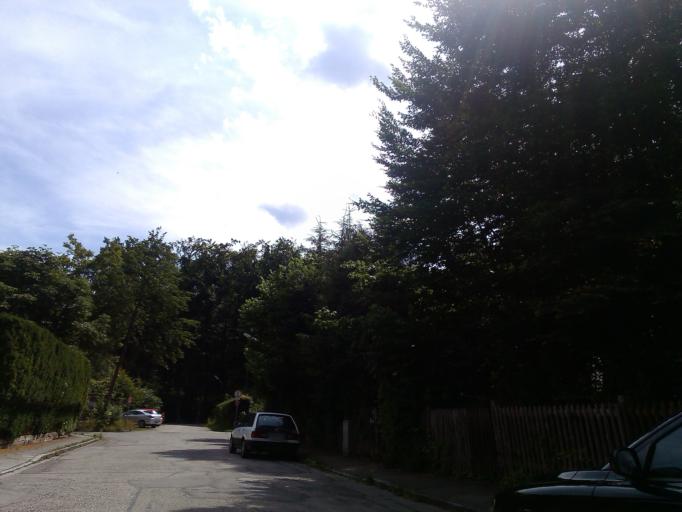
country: DE
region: Bavaria
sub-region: Upper Bavaria
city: Gauting
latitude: 48.0680
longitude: 11.3632
